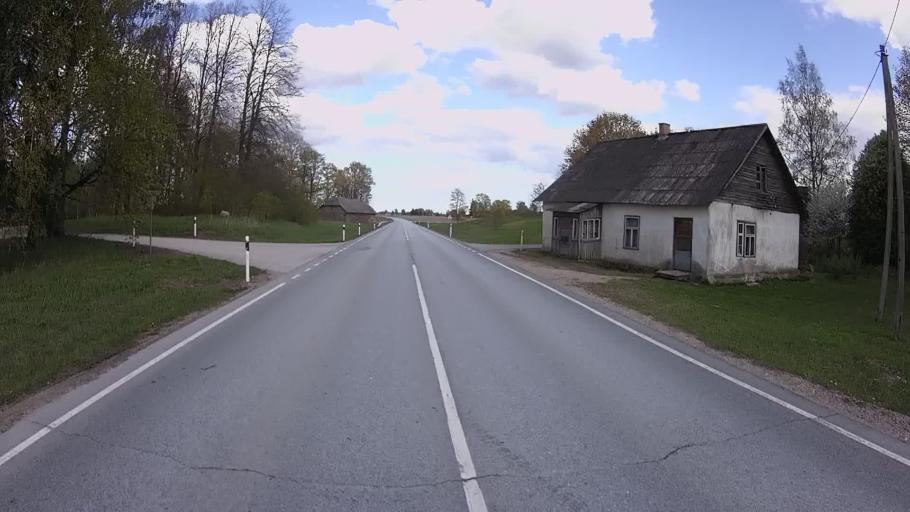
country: EE
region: Jogevamaa
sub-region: Mustvee linn
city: Mustvee
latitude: 58.8236
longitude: 26.6919
